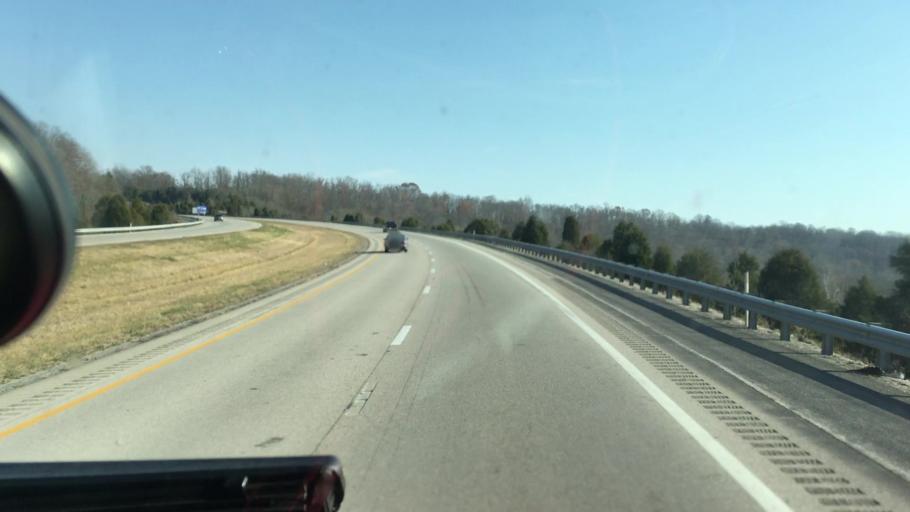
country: US
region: Kentucky
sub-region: Bath County
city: Owingsville
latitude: 38.1221
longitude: -83.7658
